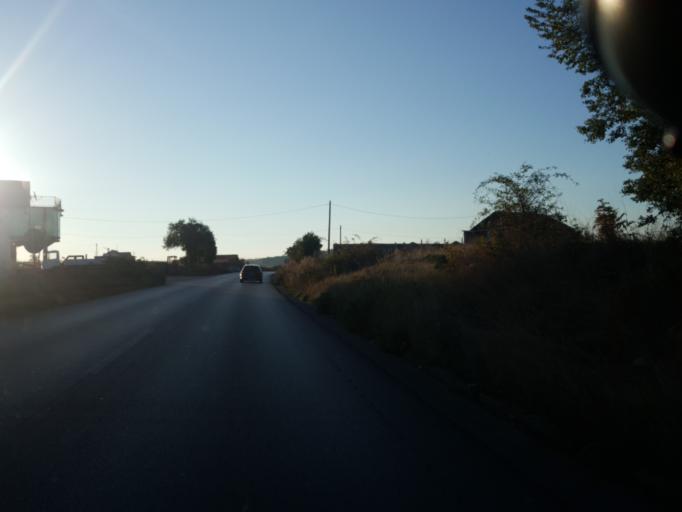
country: XK
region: Pec
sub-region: Komuna e Klines
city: Klina
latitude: 42.5937
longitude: 20.6598
